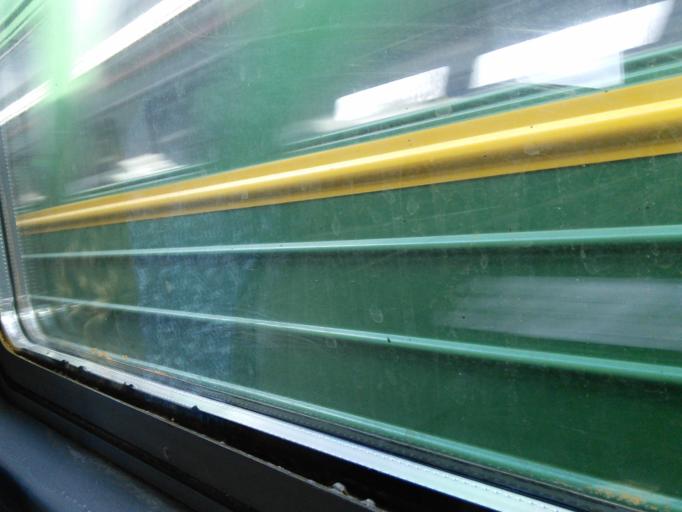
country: RU
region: Moskovskaya
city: Stolbovaya
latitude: 55.2591
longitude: 37.4974
